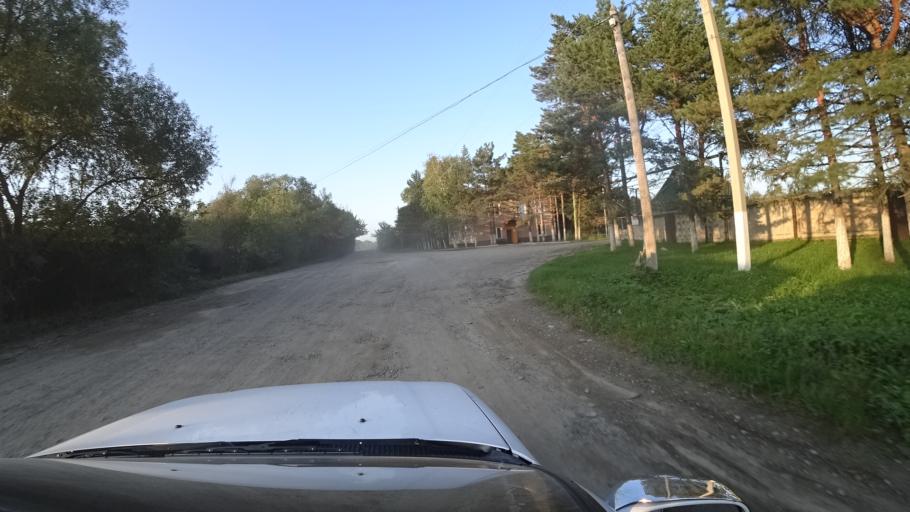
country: RU
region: Primorskiy
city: Dal'nerechensk
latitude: 45.9357
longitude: 133.7592
